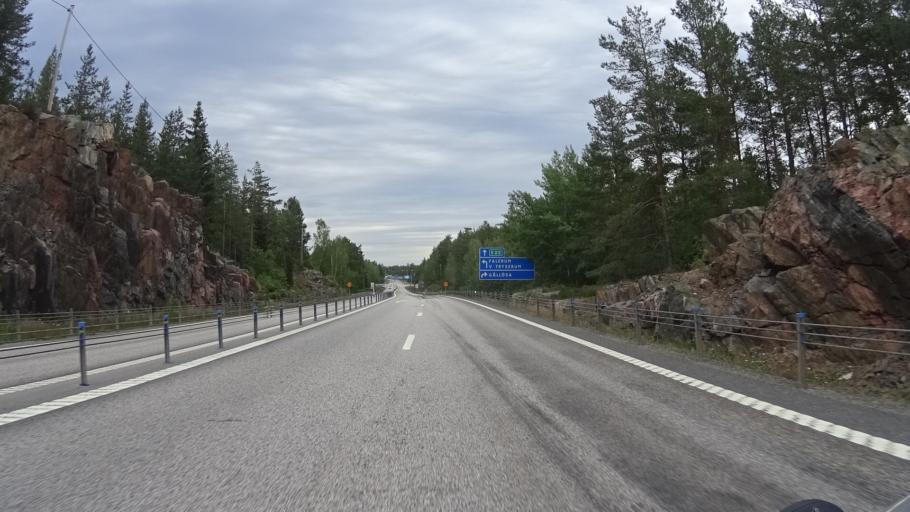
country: SE
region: OEstergoetland
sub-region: Valdemarsviks Kommun
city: Valdemarsvik
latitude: 58.1554
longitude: 16.5438
